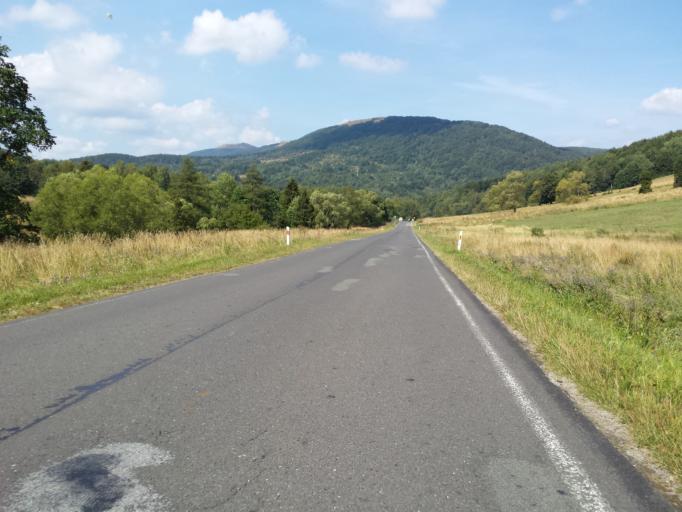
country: PL
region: Subcarpathian Voivodeship
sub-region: Powiat bieszczadzki
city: Lutowiska
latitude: 49.1324
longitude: 22.5763
